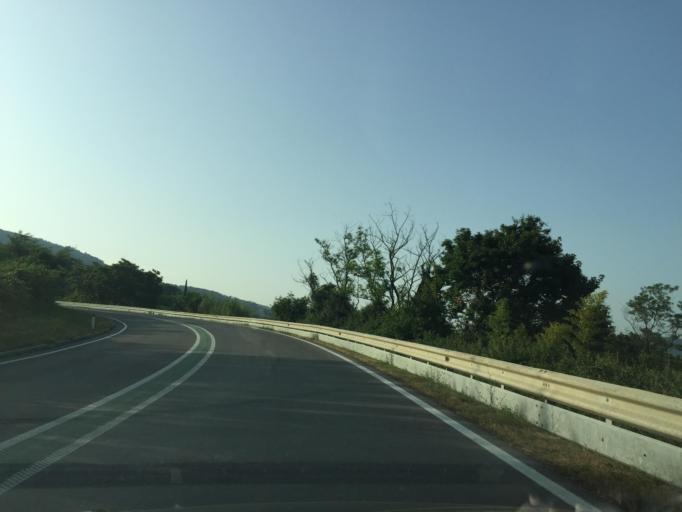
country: SI
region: Koper-Capodistria
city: Sv. Anton
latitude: 45.5495
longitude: 13.8758
